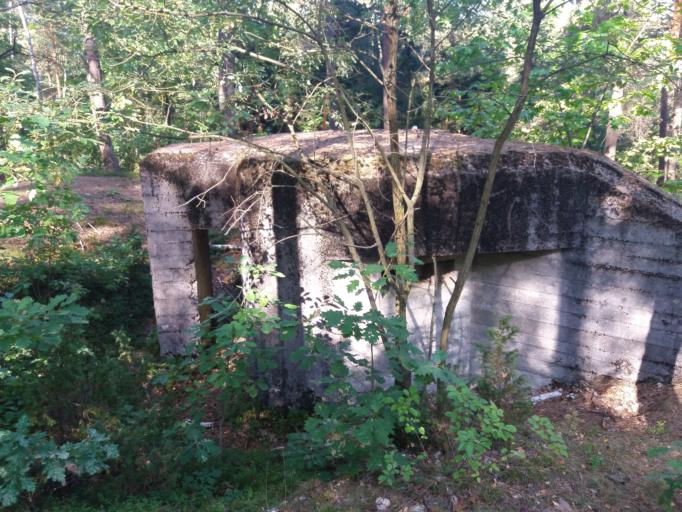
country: PL
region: Masovian Voivodeship
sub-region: Powiat mlawski
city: Mlawa
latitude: 53.1553
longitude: 20.3580
